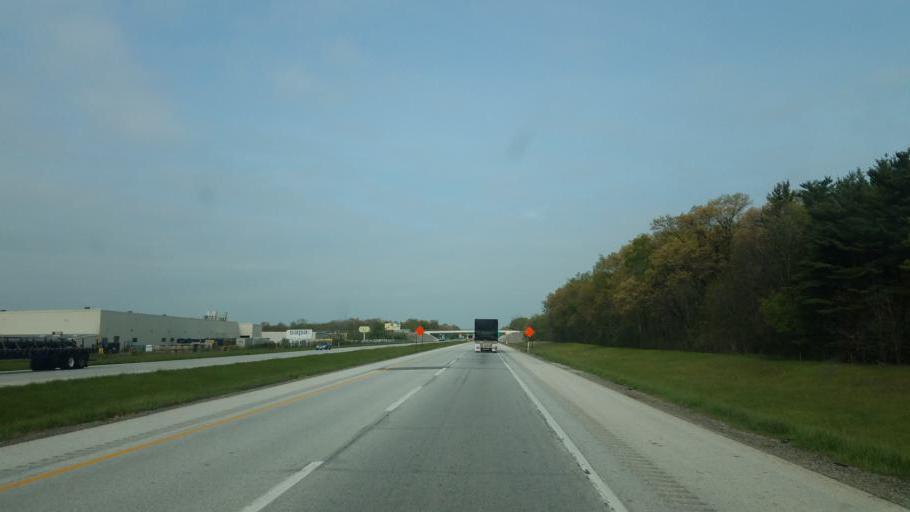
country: US
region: Indiana
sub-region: Elkhart County
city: Simonton Lake
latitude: 41.7297
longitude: -85.9211
